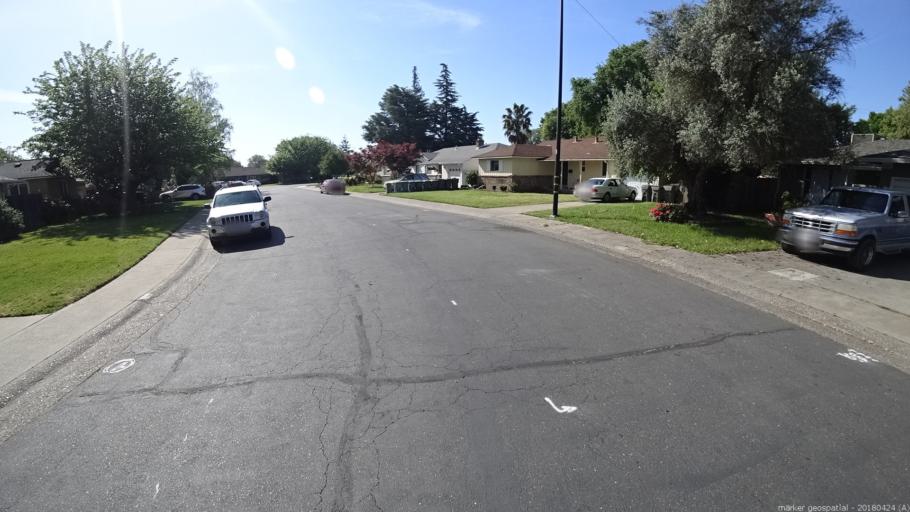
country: US
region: California
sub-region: Yolo County
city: West Sacramento
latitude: 38.5750
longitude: -121.5300
